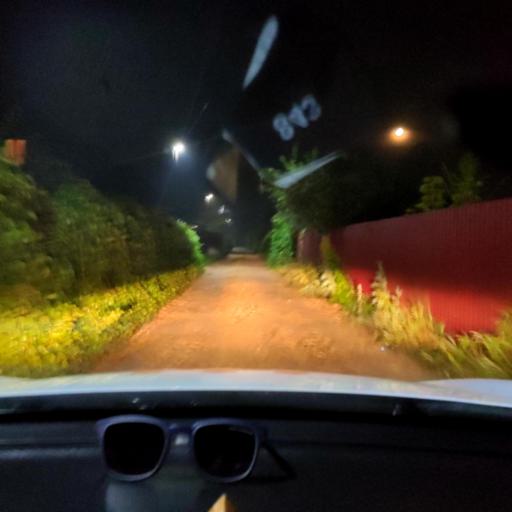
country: RU
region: Tatarstan
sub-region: Gorod Kazan'
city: Kazan
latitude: 55.8600
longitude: 49.1880
